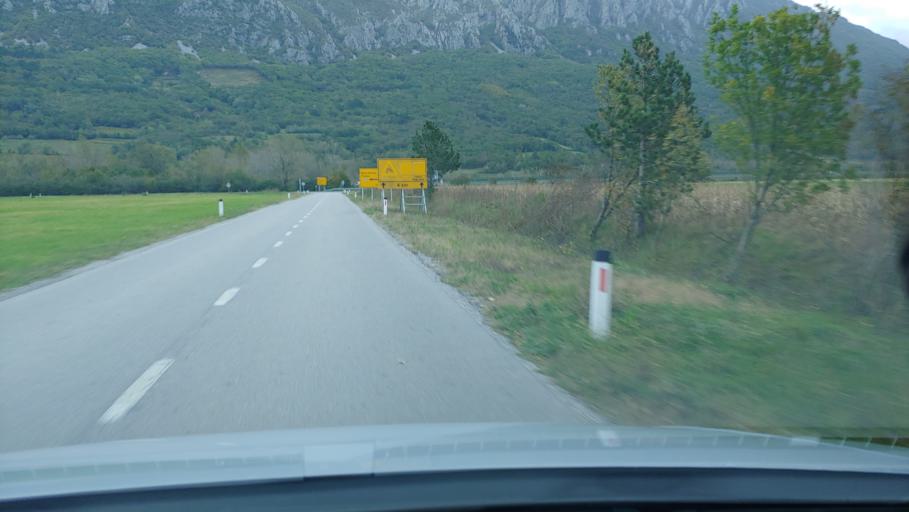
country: SI
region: Vipava
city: Vipava
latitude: 45.8248
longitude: 13.9556
